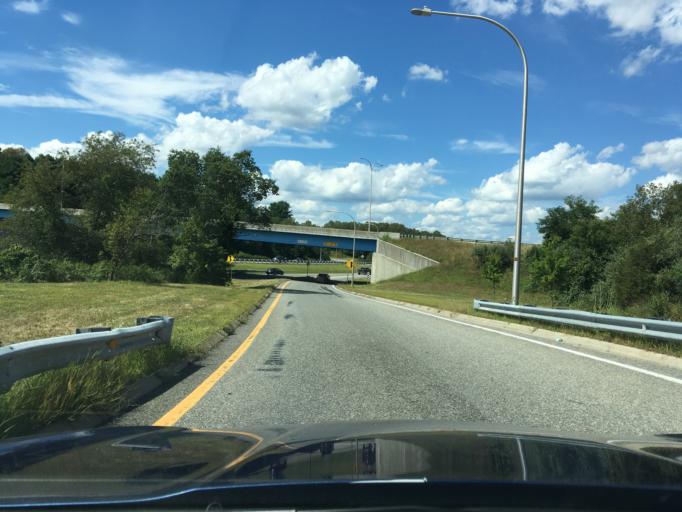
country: US
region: Rhode Island
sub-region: Kent County
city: East Greenwich
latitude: 41.6286
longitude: -71.4860
